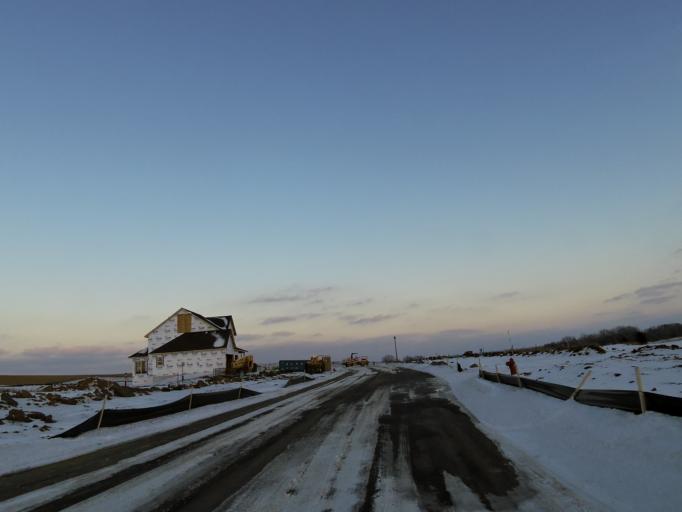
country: US
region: Minnesota
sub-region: Dakota County
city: Farmington
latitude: 44.6730
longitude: -93.1279
